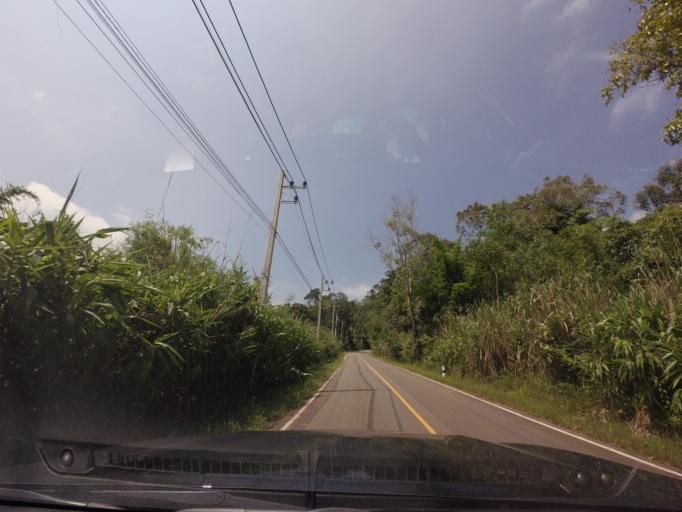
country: TH
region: Loei
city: Na Haeo
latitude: 17.4669
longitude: 100.9291
